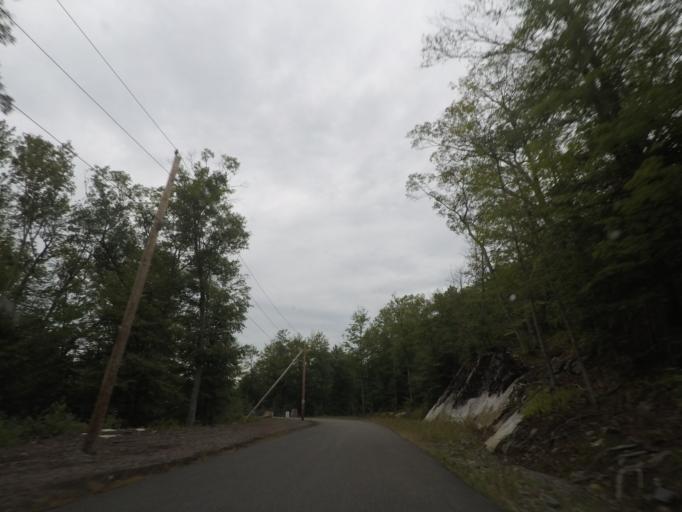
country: US
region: Massachusetts
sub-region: Hampshire County
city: Ware
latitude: 42.2305
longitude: -72.2460
